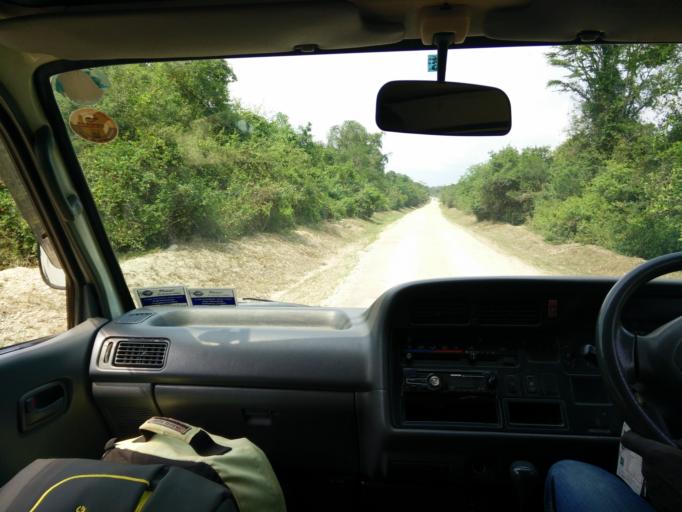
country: UG
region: Western Region
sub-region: Rubirizi District
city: Rubirizi
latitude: -0.3529
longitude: 29.8703
